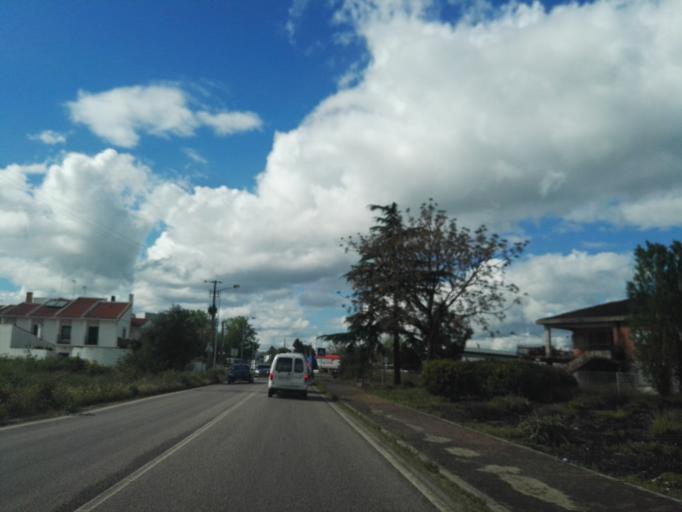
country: PT
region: Santarem
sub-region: Torres Novas
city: Riachos
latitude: 39.4628
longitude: -8.5221
